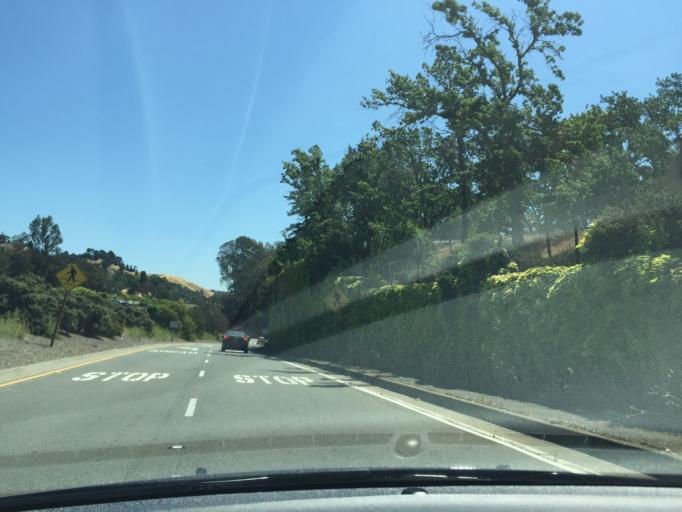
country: US
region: California
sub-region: Contra Costa County
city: Lafayette
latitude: 37.8932
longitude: -122.1229
